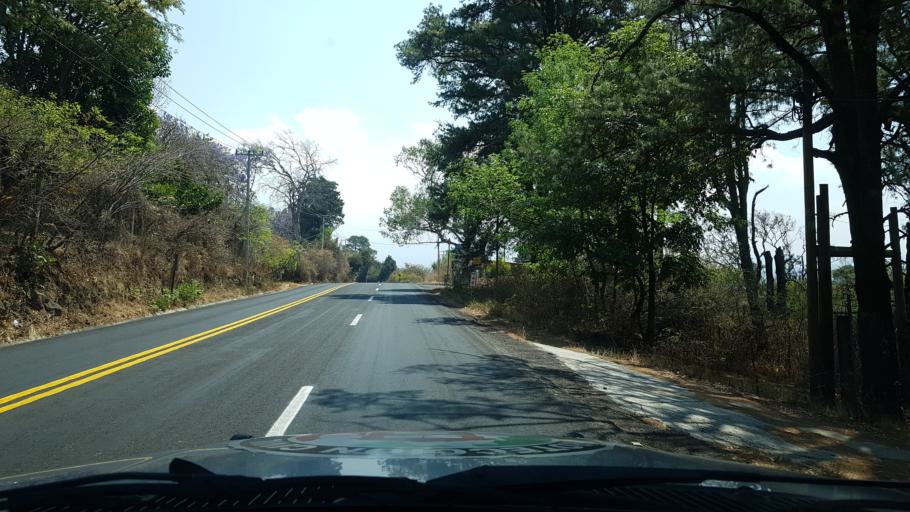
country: MX
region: Mexico
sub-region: Tepetlixpa
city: Nepantla de Sor Juana Ines de la Cruz
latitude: 18.9852
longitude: -98.8372
